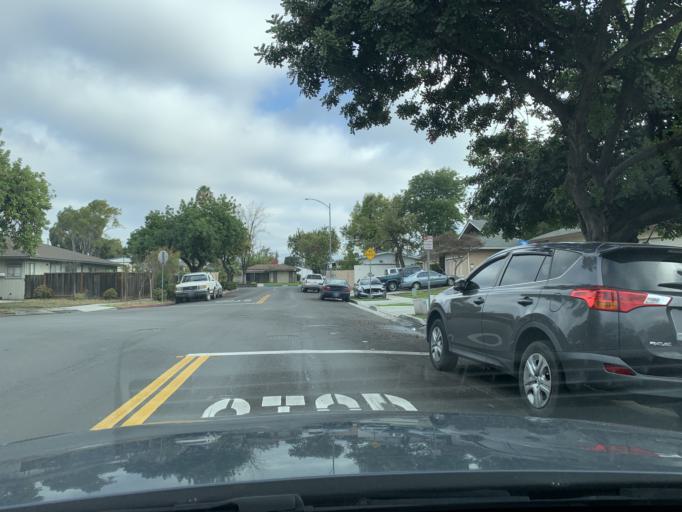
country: US
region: California
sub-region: Santa Clara County
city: Alum Rock
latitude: 37.3321
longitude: -121.8497
